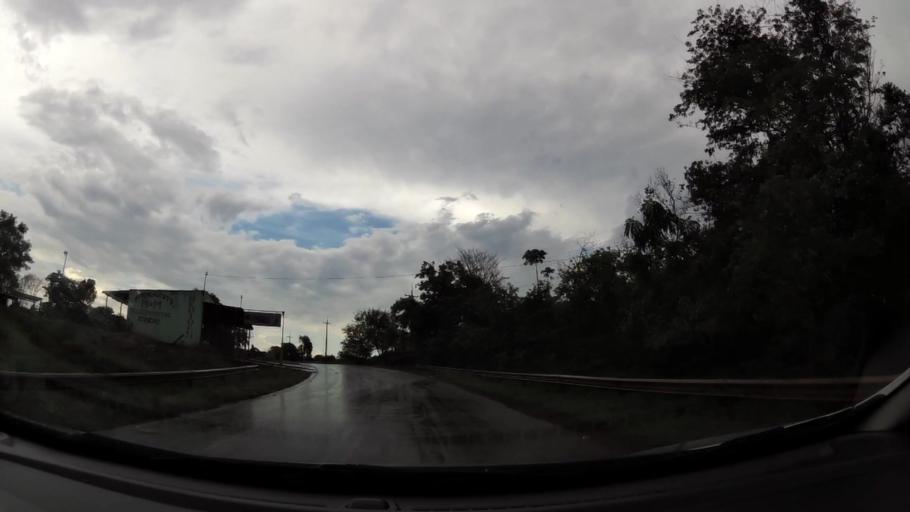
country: PY
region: Alto Parana
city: Los Cedrales
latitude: -25.5837
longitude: -54.6768
